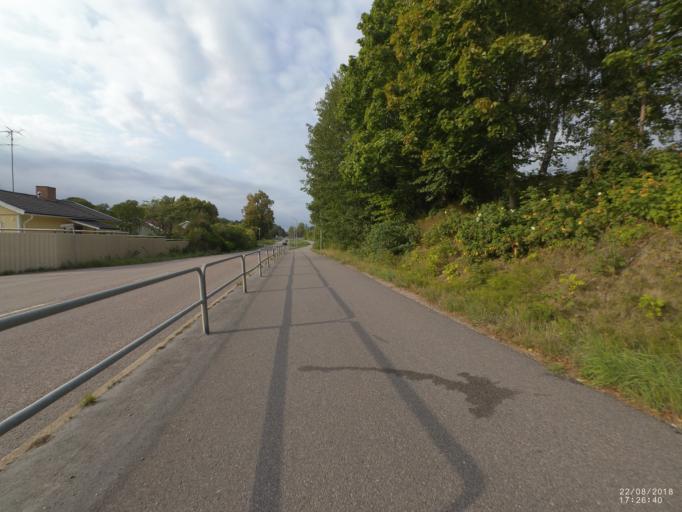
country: SE
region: Soedermanland
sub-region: Nykopings Kommun
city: Nykoping
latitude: 58.7628
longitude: 17.0087
